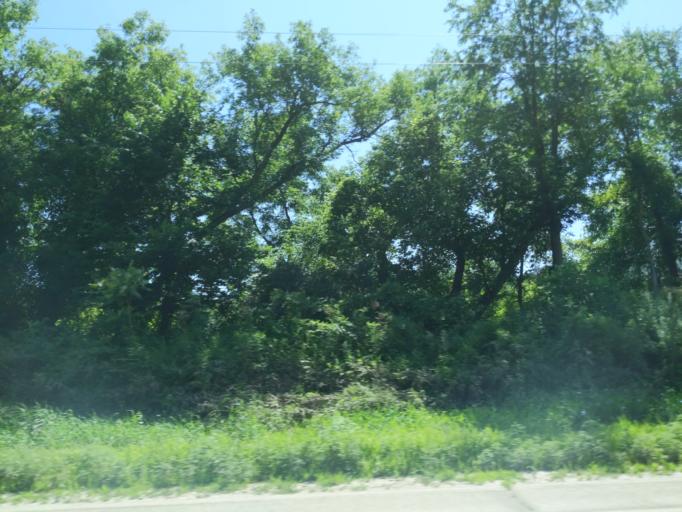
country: US
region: Wisconsin
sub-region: Vernon County
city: Westby
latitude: 43.6958
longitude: -91.0415
